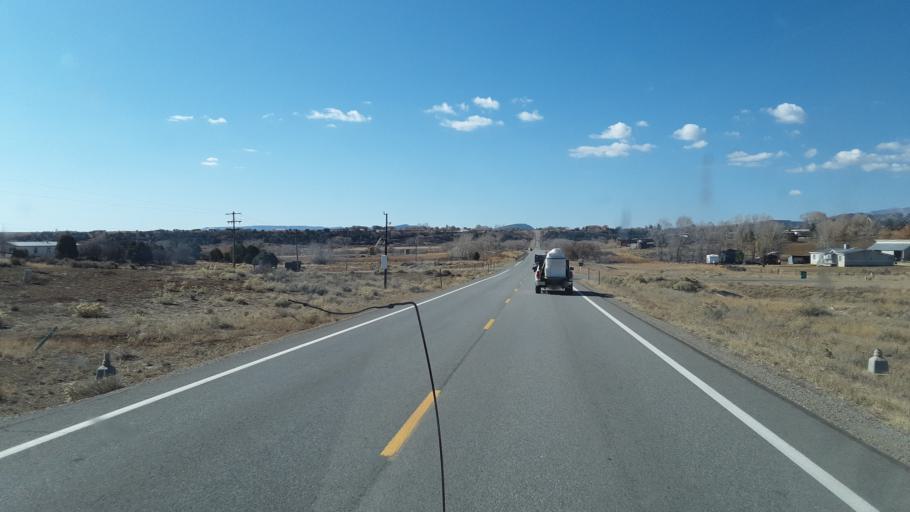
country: US
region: Colorado
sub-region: La Plata County
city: Bayfield
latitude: 37.2292
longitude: -107.7421
